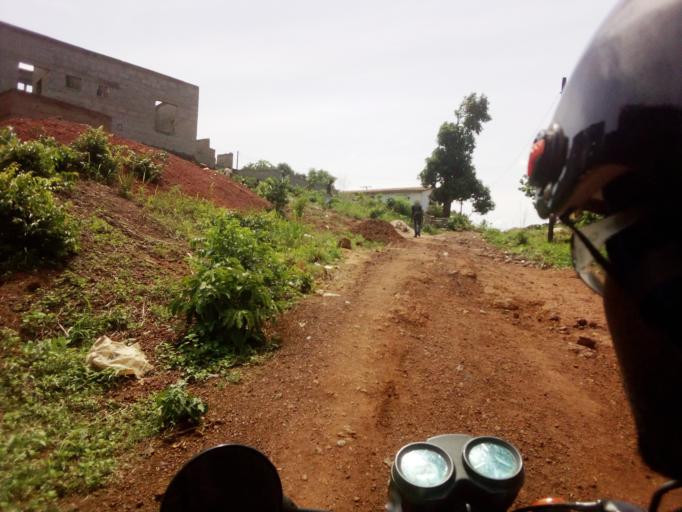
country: SL
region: Western Area
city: Waterloo
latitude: 8.3453
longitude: -13.0738
